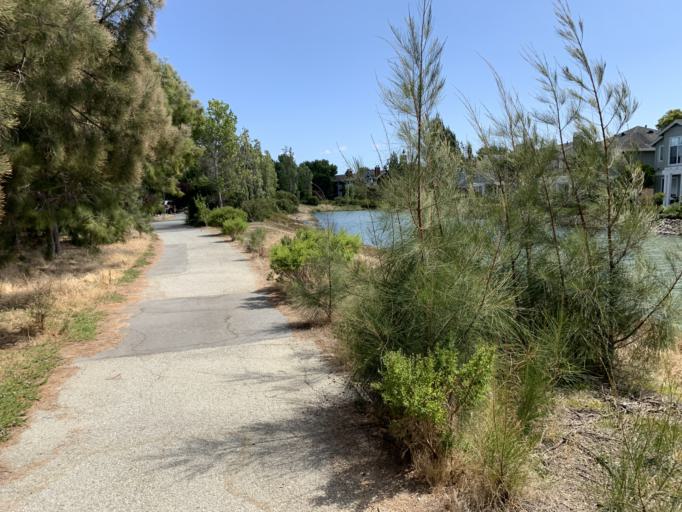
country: US
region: California
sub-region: San Mateo County
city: Redwood Shores
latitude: 37.5454
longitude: -122.2343
